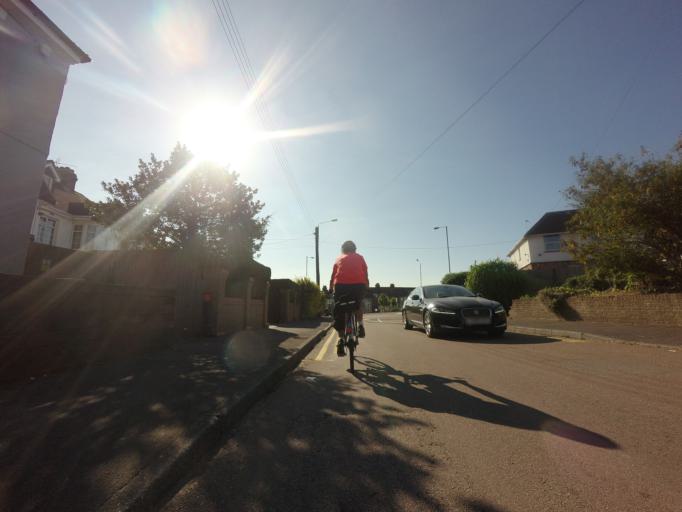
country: GB
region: England
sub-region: Kent
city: Strood
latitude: 51.4128
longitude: 0.5119
